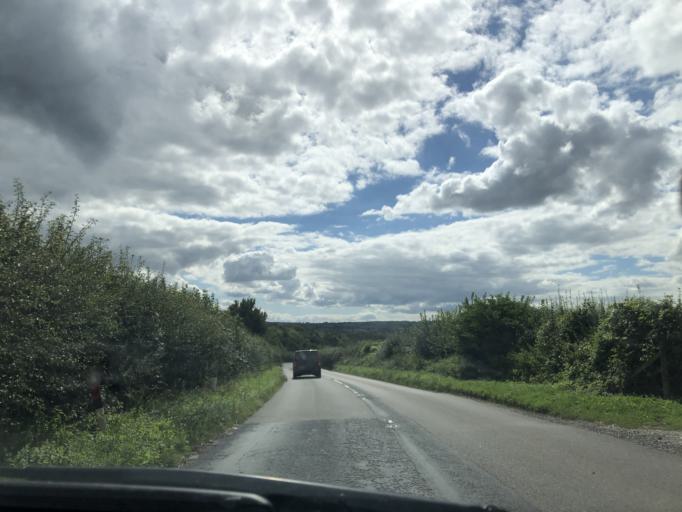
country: GB
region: England
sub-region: Kent
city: Halstead
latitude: 51.3003
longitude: 0.1436
